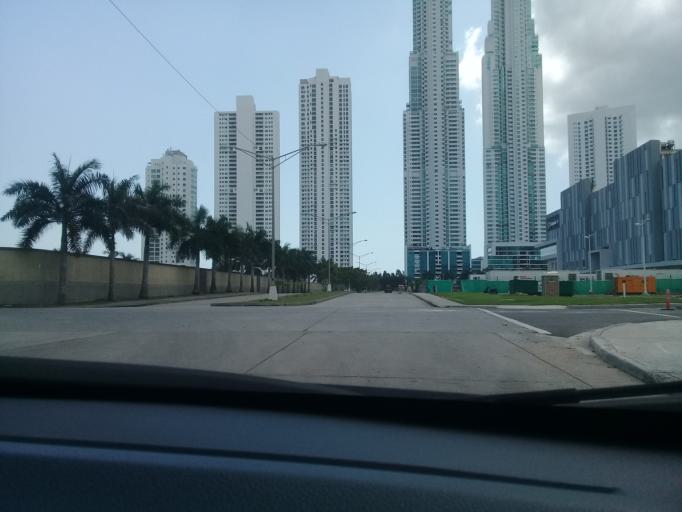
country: PA
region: Panama
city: San Miguelito
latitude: 9.0150
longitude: -79.4640
